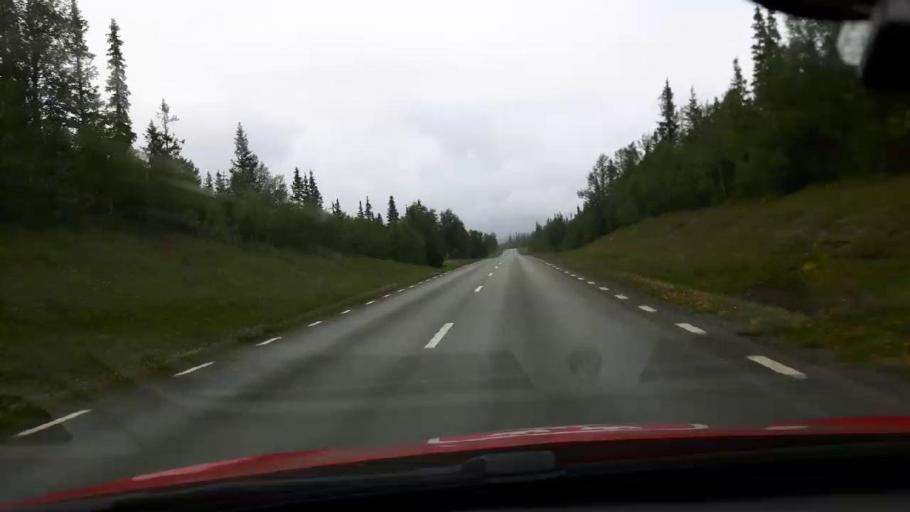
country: NO
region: Nord-Trondelag
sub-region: Meraker
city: Meraker
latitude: 63.2709
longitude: 12.1519
